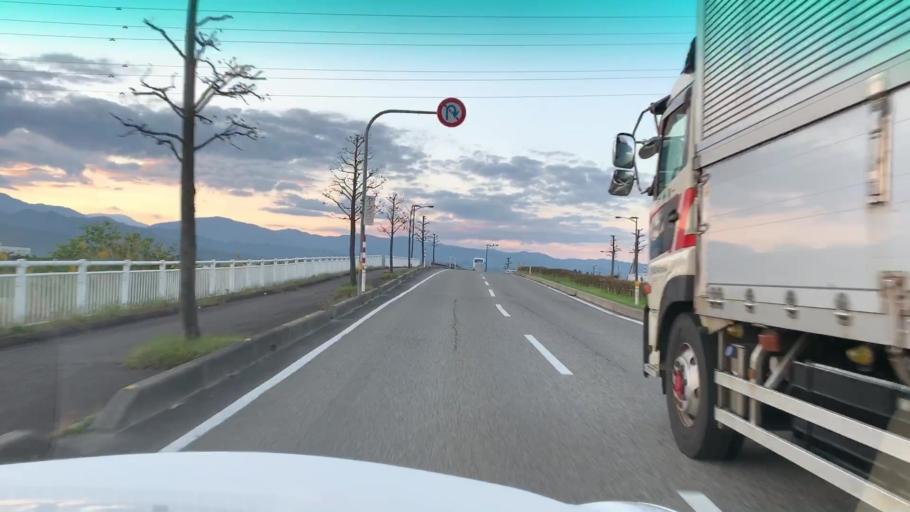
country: JP
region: Toyama
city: Kamiichi
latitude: 36.6955
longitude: 137.3429
